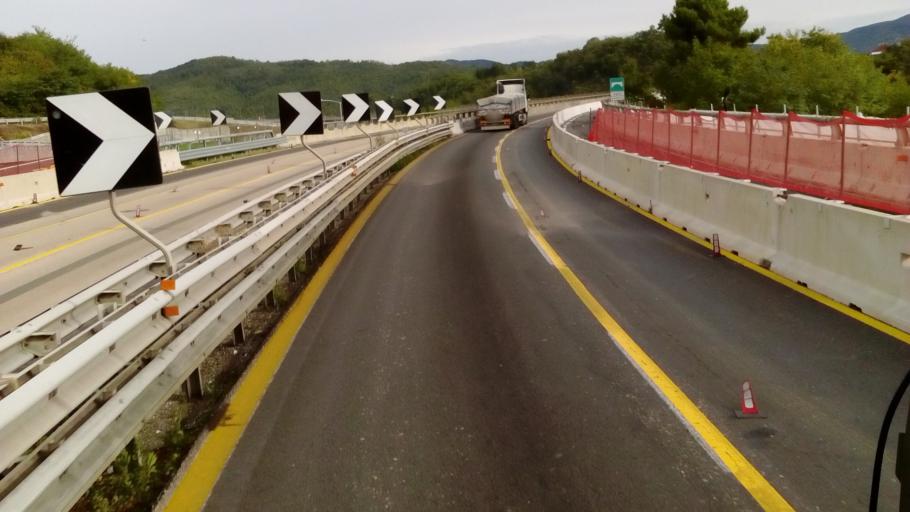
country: IT
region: Tuscany
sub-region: Province of Florence
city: Barberino di Mugello
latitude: 44.0249
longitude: 11.2219
